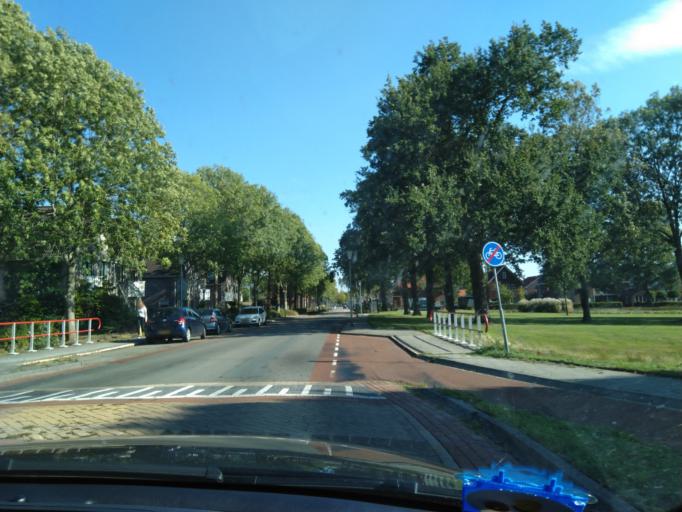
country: NL
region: Groningen
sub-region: Gemeente Veendam
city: Veendam
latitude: 53.0871
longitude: 6.8601
